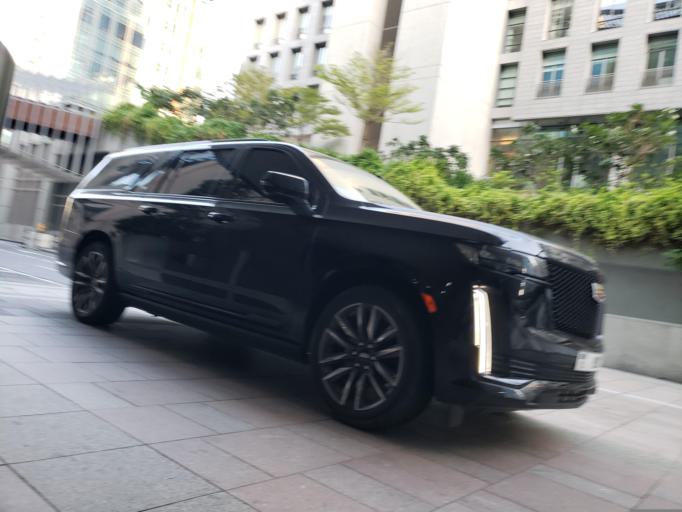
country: AE
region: Ash Shariqah
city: Sharjah
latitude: 25.2138
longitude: 55.2819
